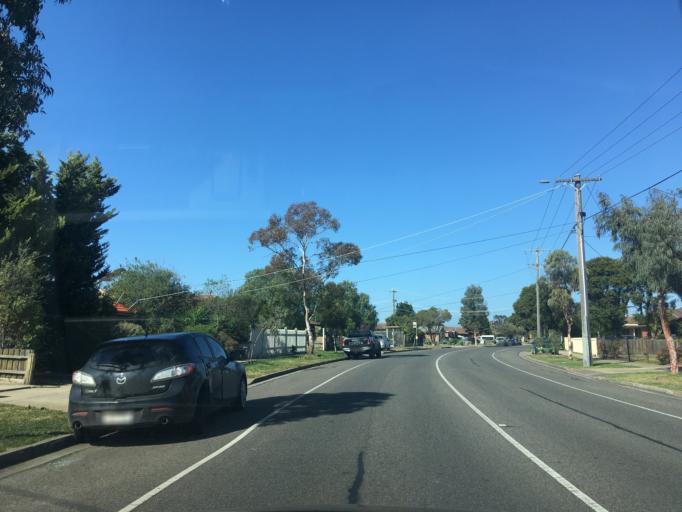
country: AU
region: Victoria
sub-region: Wyndham
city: Hoppers Crossing
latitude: -37.8725
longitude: 144.7097
